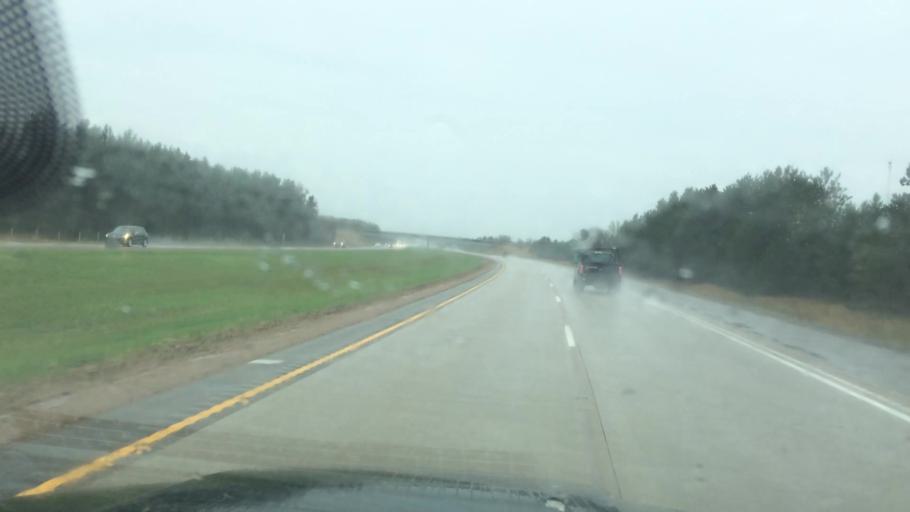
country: US
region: Wisconsin
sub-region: Portage County
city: Stevens Point
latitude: 44.6319
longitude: -89.6351
